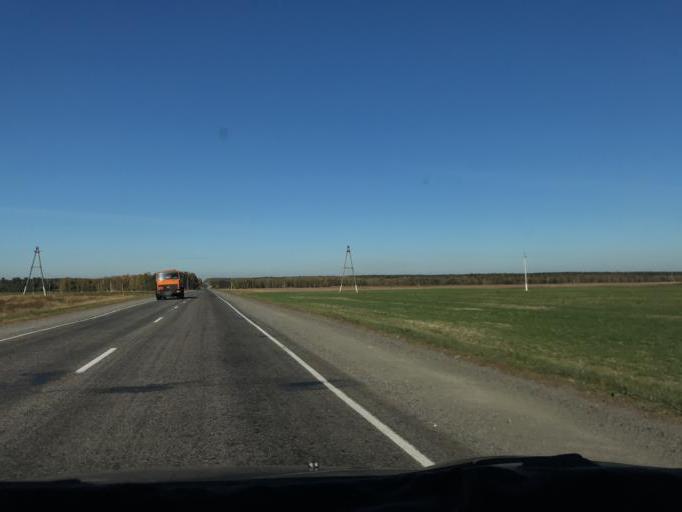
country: BY
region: Gomel
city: Yel'sk
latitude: 51.7747
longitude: 29.1909
